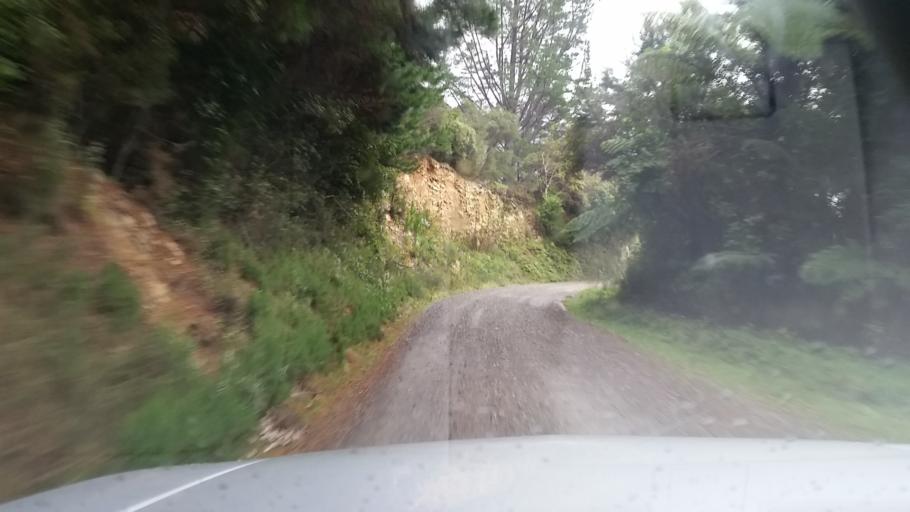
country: NZ
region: Marlborough
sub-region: Marlborough District
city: Picton
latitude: -41.1339
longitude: 174.0428
